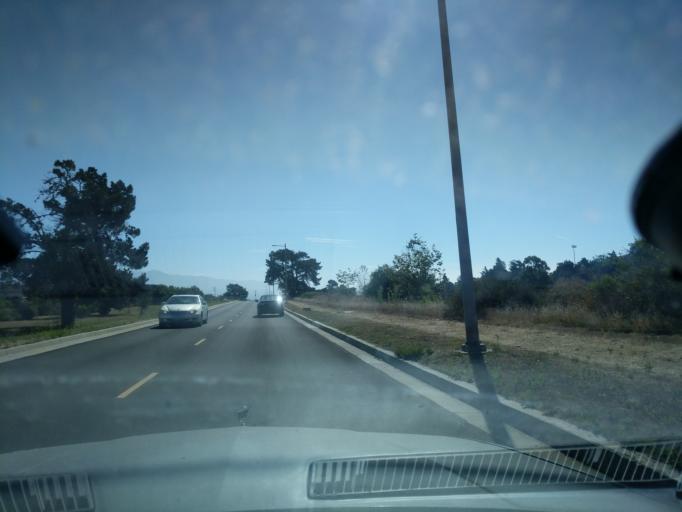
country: US
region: California
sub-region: Santa Barbara County
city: Isla Vista
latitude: 34.4222
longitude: -119.8585
